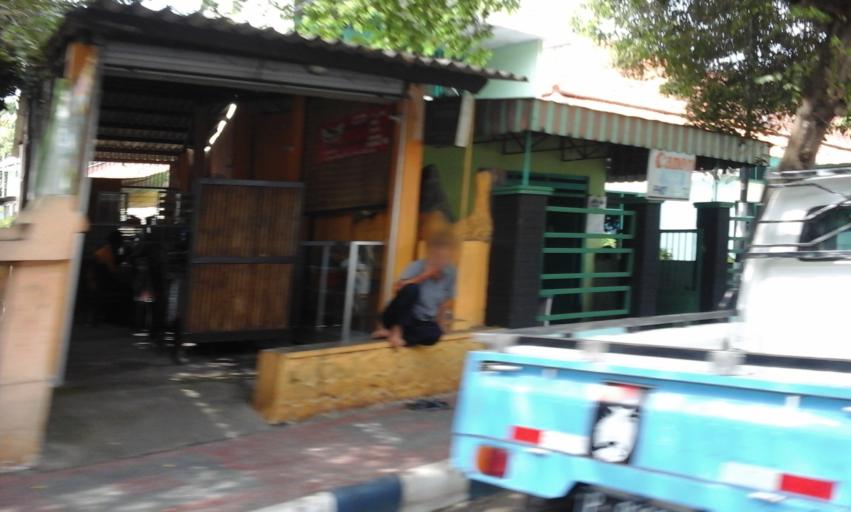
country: ID
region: East Java
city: Banyuwangi
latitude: -8.2349
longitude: 114.3591
